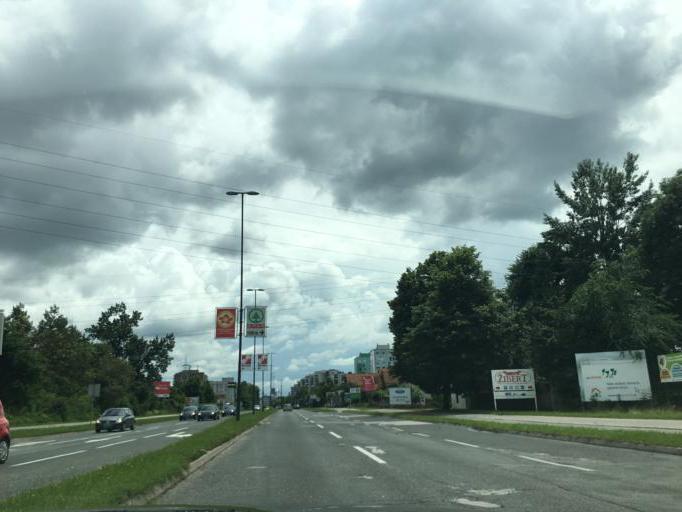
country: SI
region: Ljubljana
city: Ljubljana
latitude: 46.0899
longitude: 14.4718
